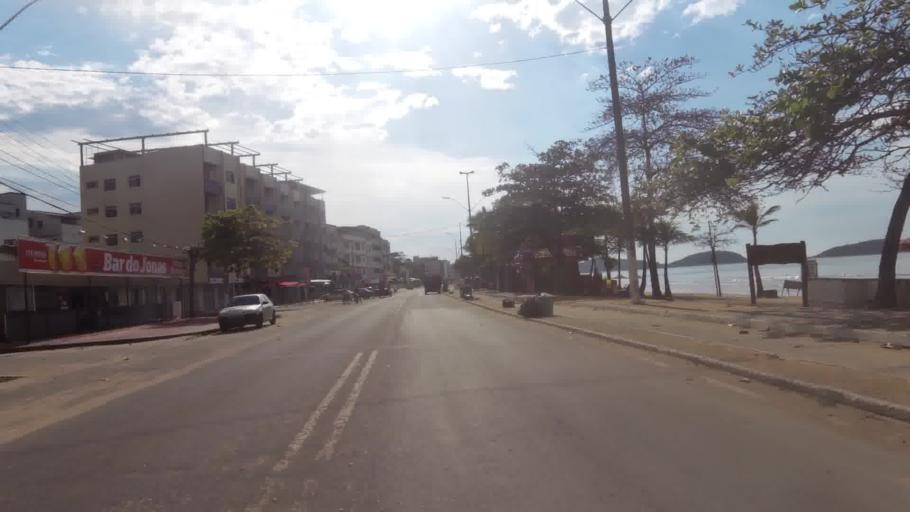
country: BR
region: Espirito Santo
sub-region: Piuma
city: Piuma
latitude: -20.8476
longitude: -40.7437
